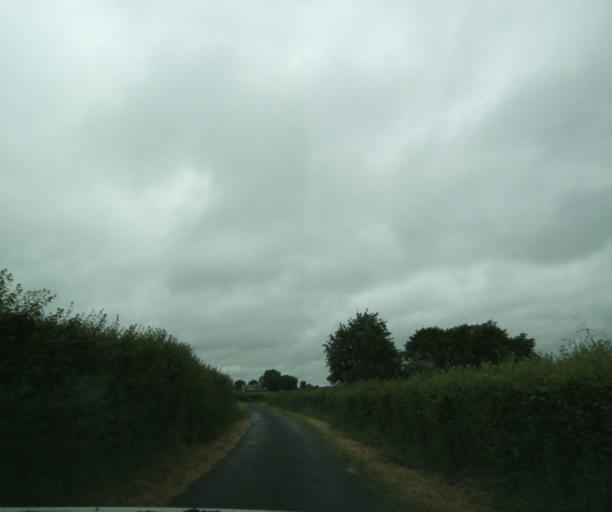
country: FR
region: Bourgogne
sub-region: Departement de Saone-et-Loire
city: Palinges
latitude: 46.5589
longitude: 4.2008
